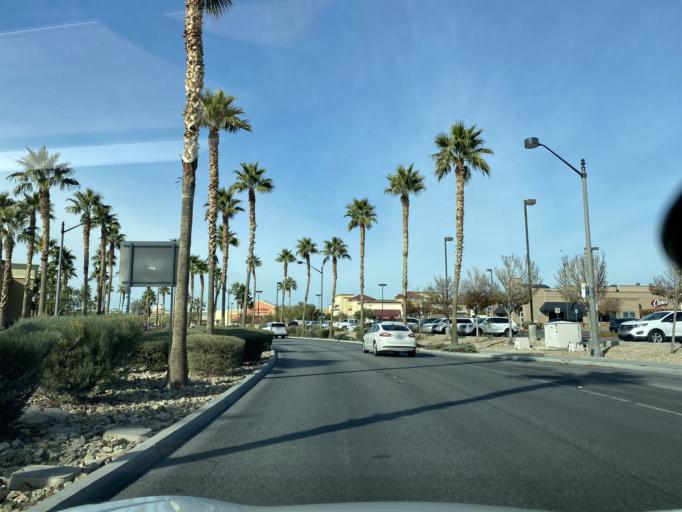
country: US
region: Nevada
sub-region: Clark County
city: Las Vegas
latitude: 36.2642
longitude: -115.2568
